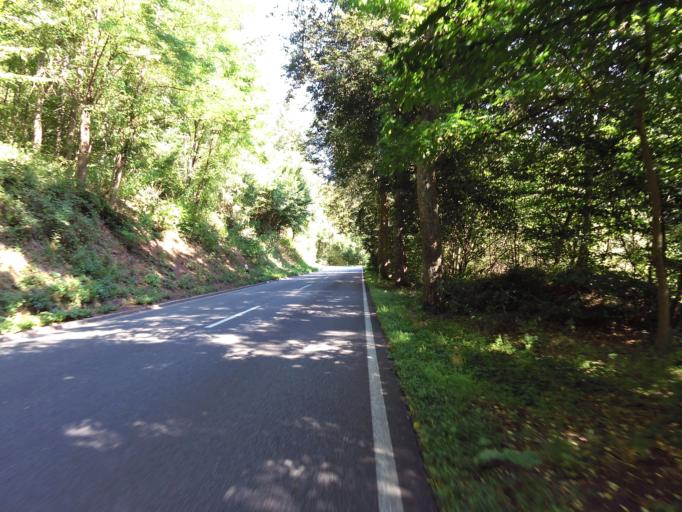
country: DE
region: Rheinland-Pfalz
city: Frankeneck
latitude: 49.3698
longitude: 8.0304
